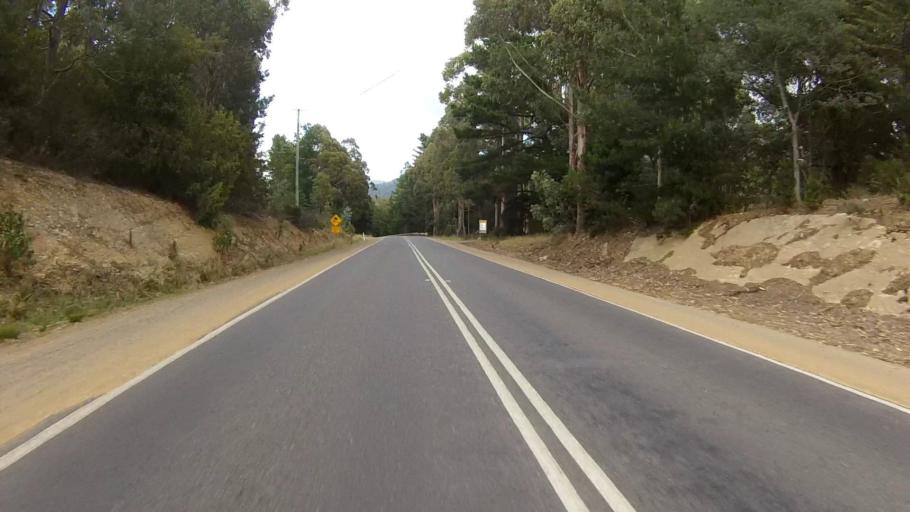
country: AU
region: Tasmania
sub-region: Kingborough
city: Kettering
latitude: -43.0945
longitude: 147.2444
